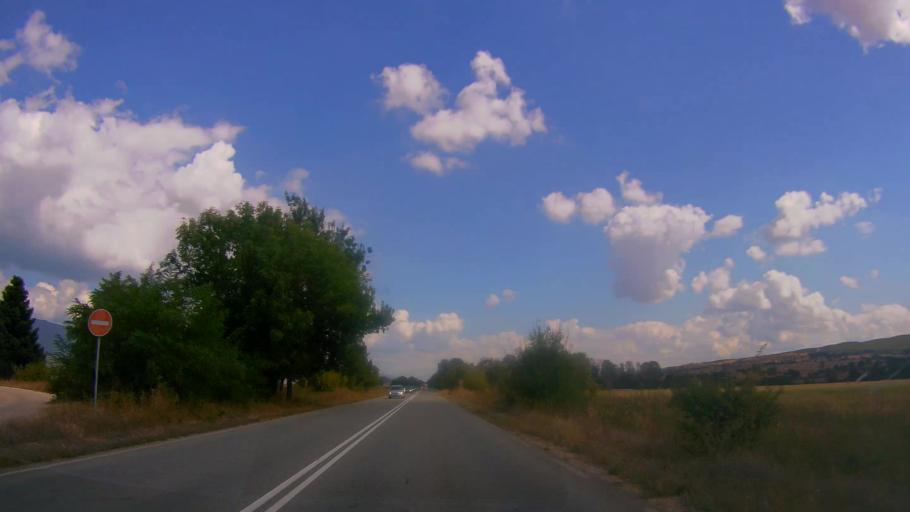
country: BG
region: Sliven
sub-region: Obshtina Tvurditsa
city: Tvurditsa
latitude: 42.6567
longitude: 25.8983
